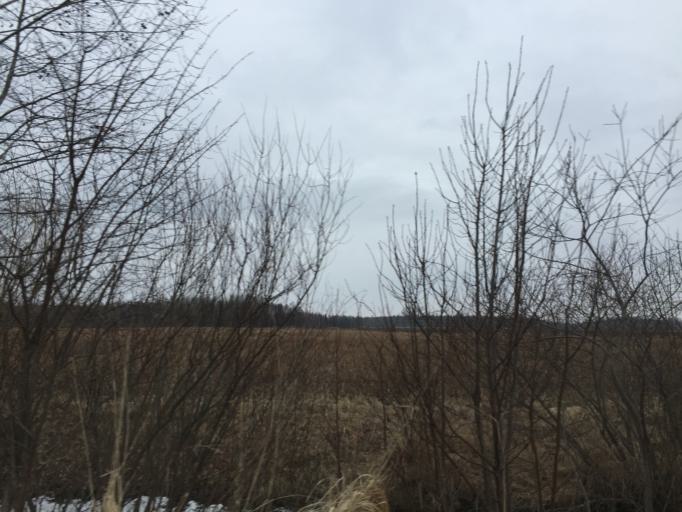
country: LV
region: Lielvarde
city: Lielvarde
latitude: 56.7579
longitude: 24.8347
